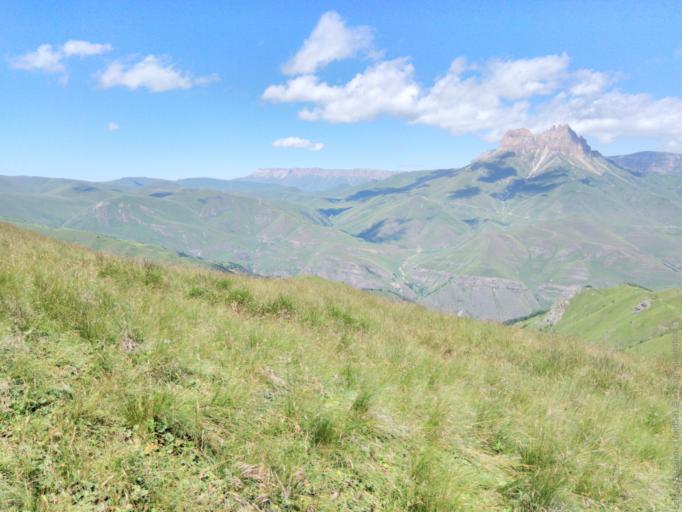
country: RU
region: Kabardino-Balkariya
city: Tyrnyauz
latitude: 43.4340
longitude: 42.9024
